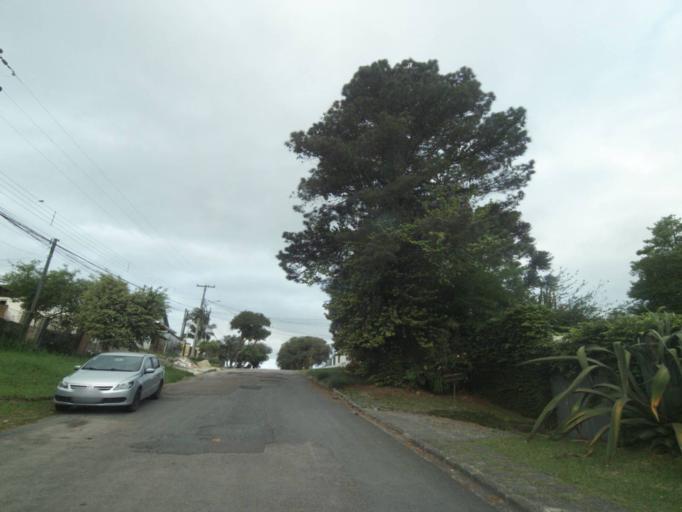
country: BR
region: Parana
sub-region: Pinhais
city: Pinhais
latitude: -25.4147
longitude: -49.2167
